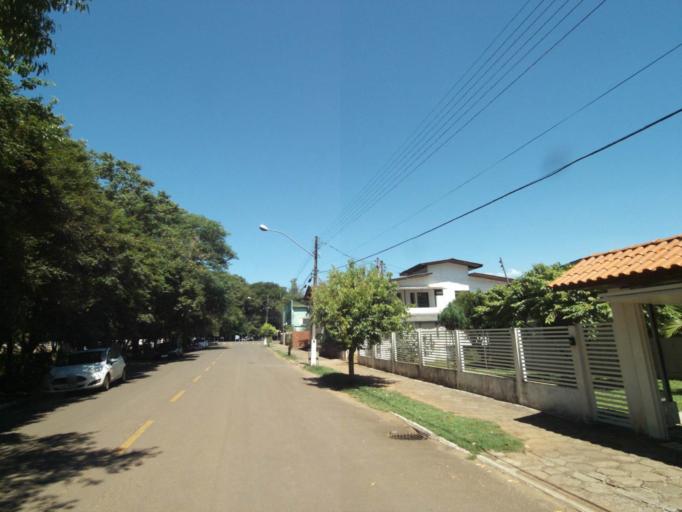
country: BR
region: Parana
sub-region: Ampere
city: Ampere
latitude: -26.1717
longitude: -53.3629
